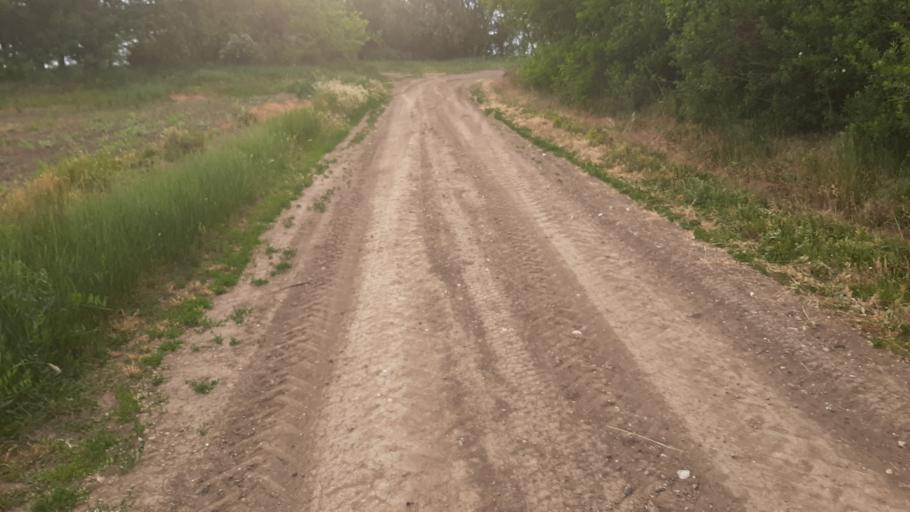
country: HU
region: Csongrad
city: Deszk
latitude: 46.1685
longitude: 20.1789
